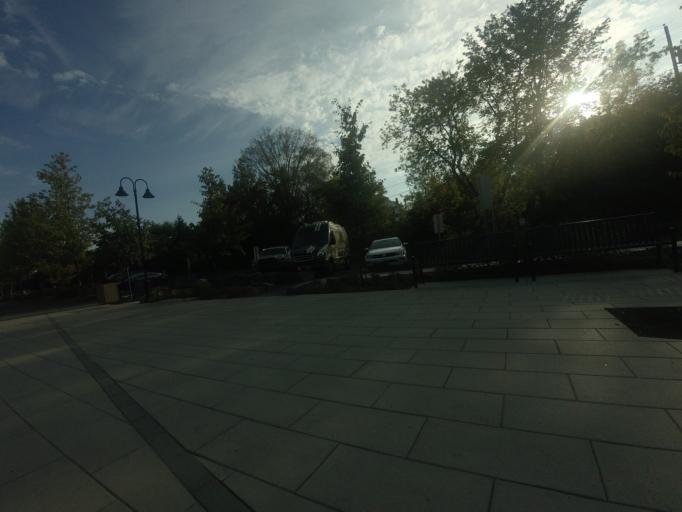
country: CA
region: Quebec
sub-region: Laurentides
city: Sainte-Adele
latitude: 45.9396
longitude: -74.1194
